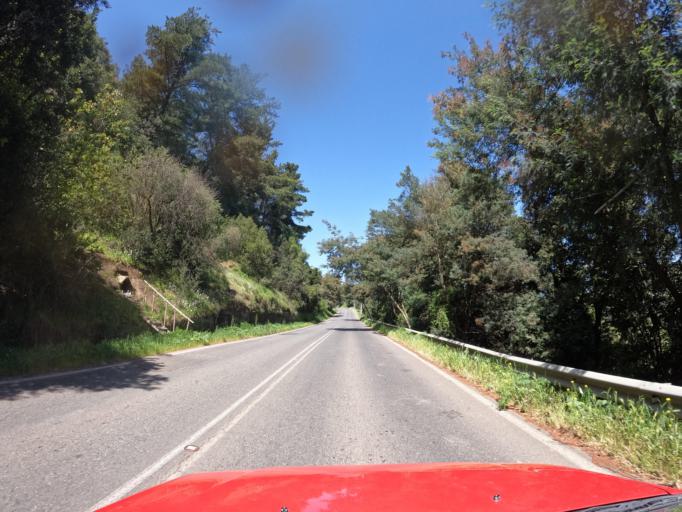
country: CL
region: Maule
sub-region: Provincia de Talca
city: San Clemente
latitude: -35.4871
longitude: -71.2892
